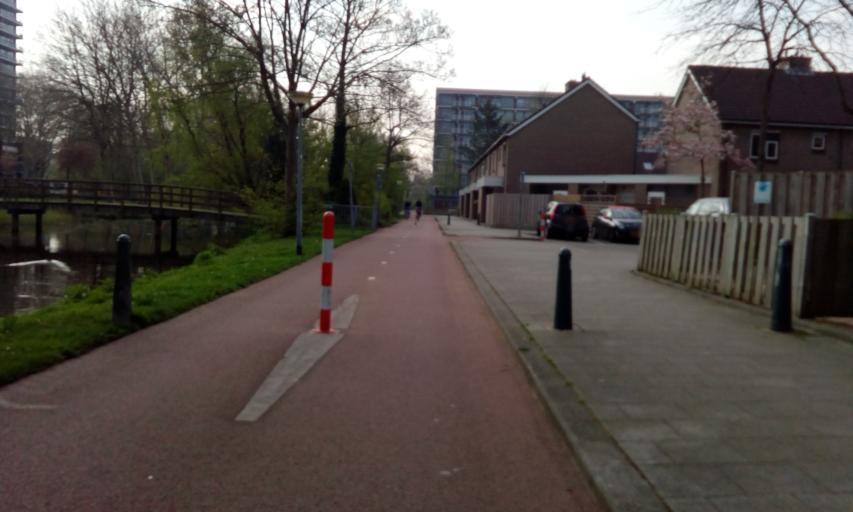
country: NL
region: South Holland
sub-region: Gemeente Rotterdam
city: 's-Gravenland
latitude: 51.9638
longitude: 4.5462
